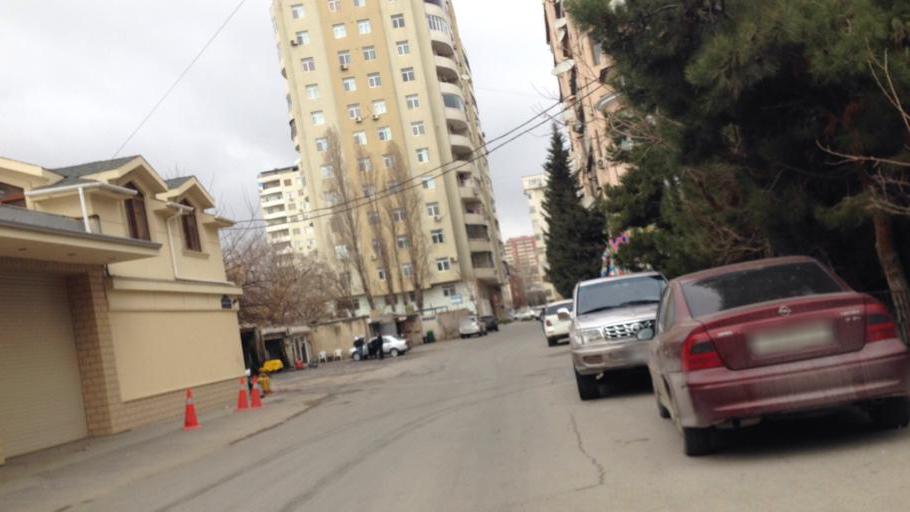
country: AZ
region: Baki
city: Bilajari
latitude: 40.4099
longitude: 49.8443
